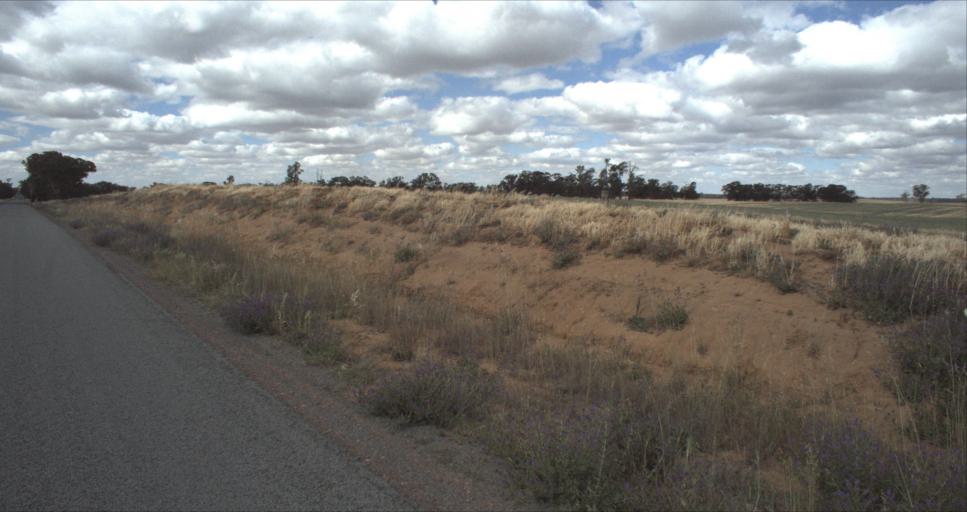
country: AU
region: New South Wales
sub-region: Leeton
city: Leeton
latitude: -34.6742
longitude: 146.3468
